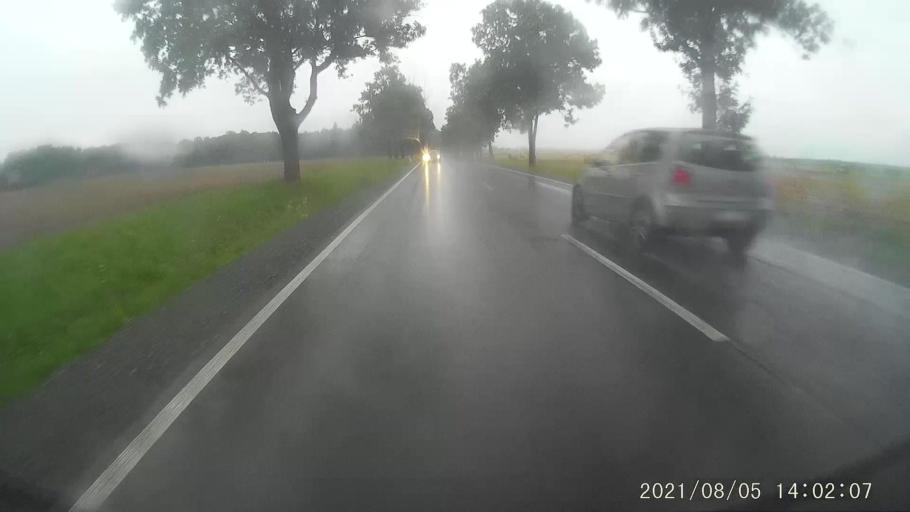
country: PL
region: Opole Voivodeship
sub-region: Powiat krapkowicki
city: Strzeleczki
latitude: 50.4532
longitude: 17.8807
